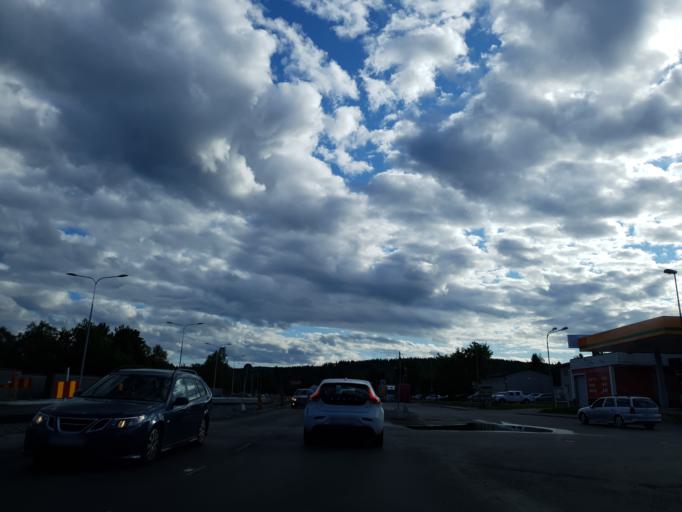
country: SE
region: Vaesternorrland
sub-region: Haernoesands Kommun
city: Haernoesand
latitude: 62.6760
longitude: 17.8420
